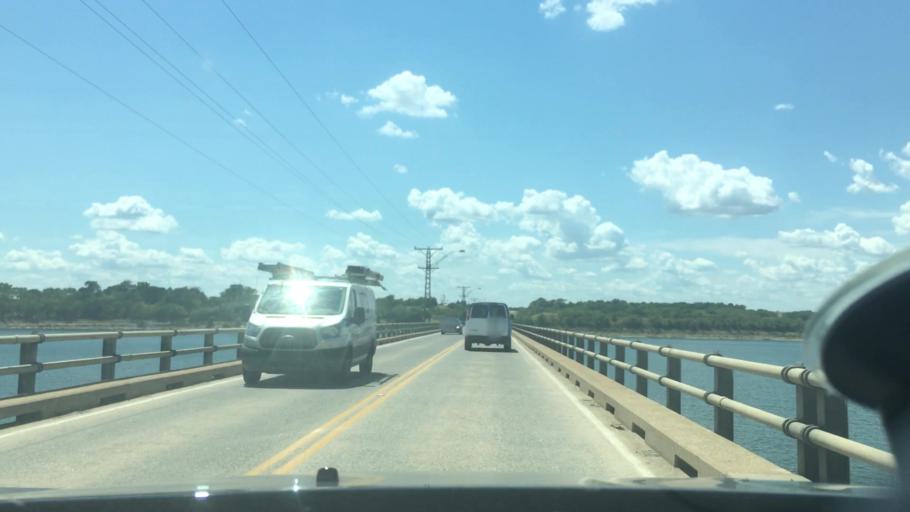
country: US
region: Oklahoma
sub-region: Marshall County
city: Kingston
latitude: 34.0000
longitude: -96.6262
